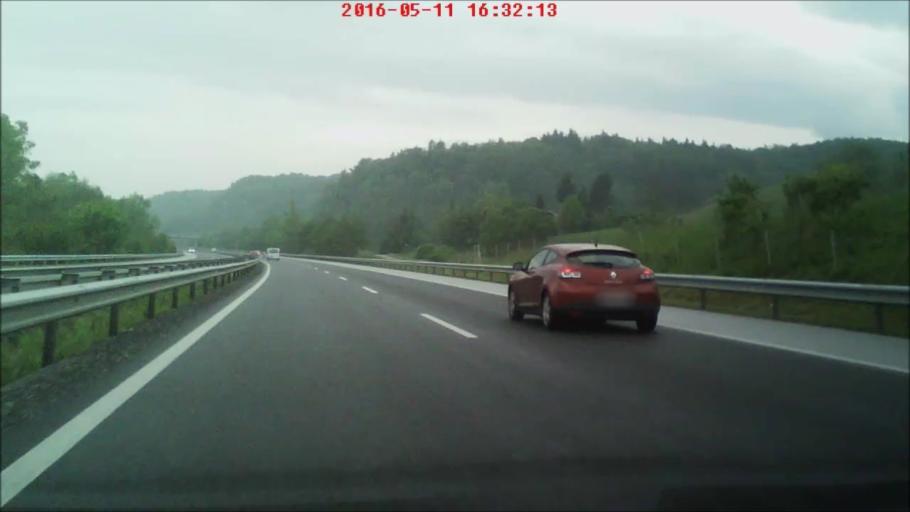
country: SI
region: Sentilj
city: Sentilj v Slov. Goricah
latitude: 46.6505
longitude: 15.6487
